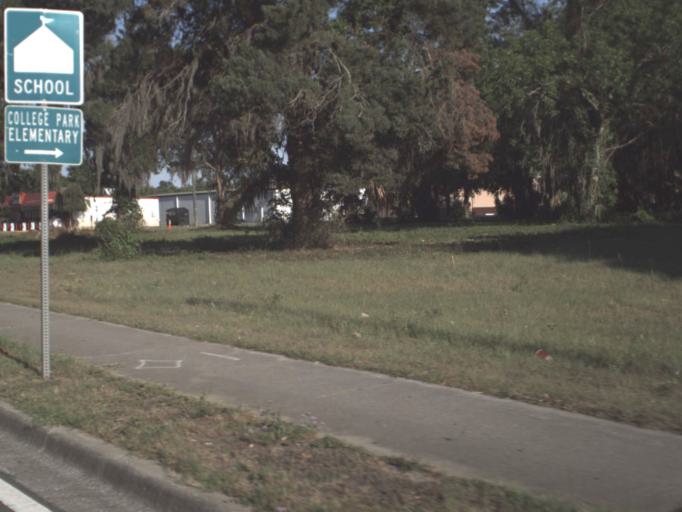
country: US
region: Florida
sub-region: Marion County
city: Ocala
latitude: 29.1862
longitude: -82.1779
